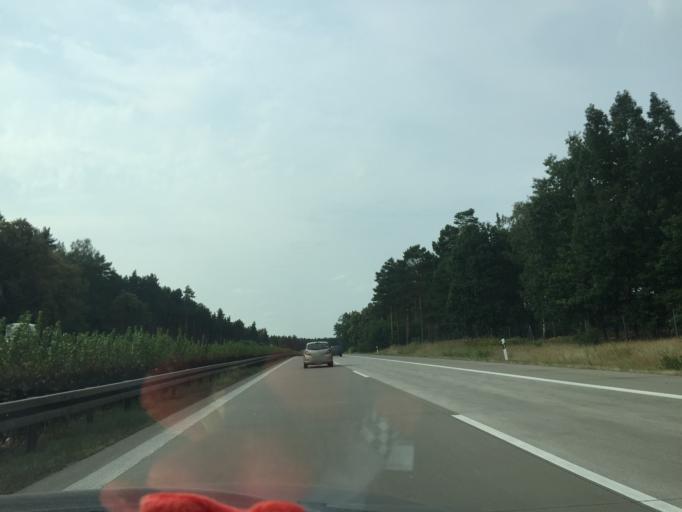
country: DE
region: Brandenburg
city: Schwerin
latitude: 52.1832
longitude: 13.6197
